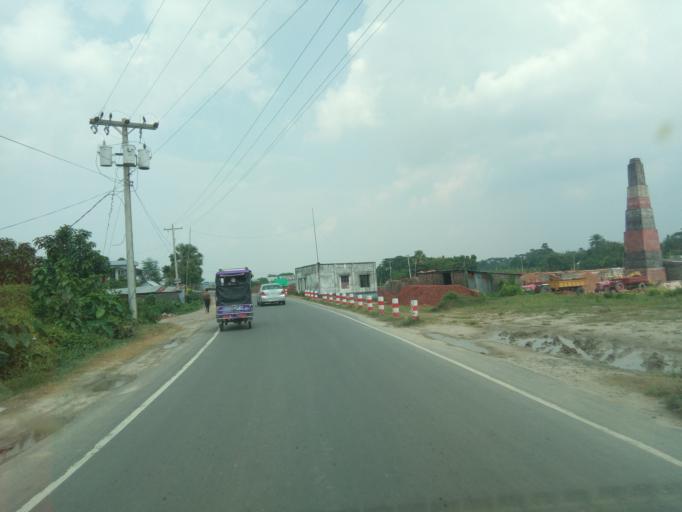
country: BD
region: Dhaka
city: Char Bhadrasan
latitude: 23.4142
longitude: 90.2162
